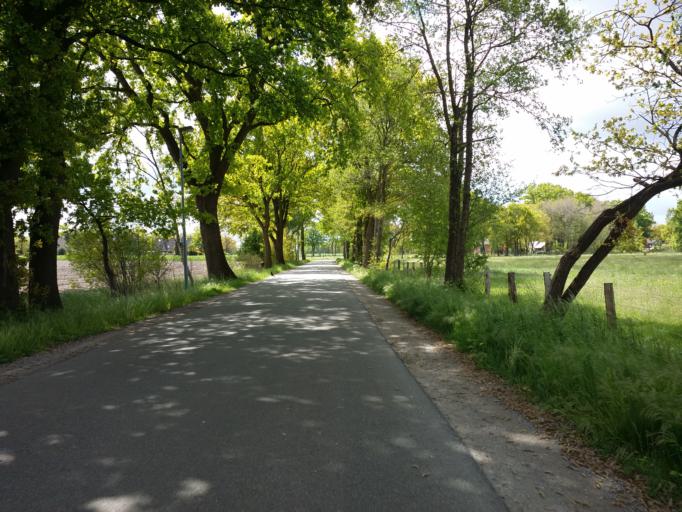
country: DE
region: Lower Saxony
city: Kirchseelte
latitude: 52.9956
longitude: 8.7004
